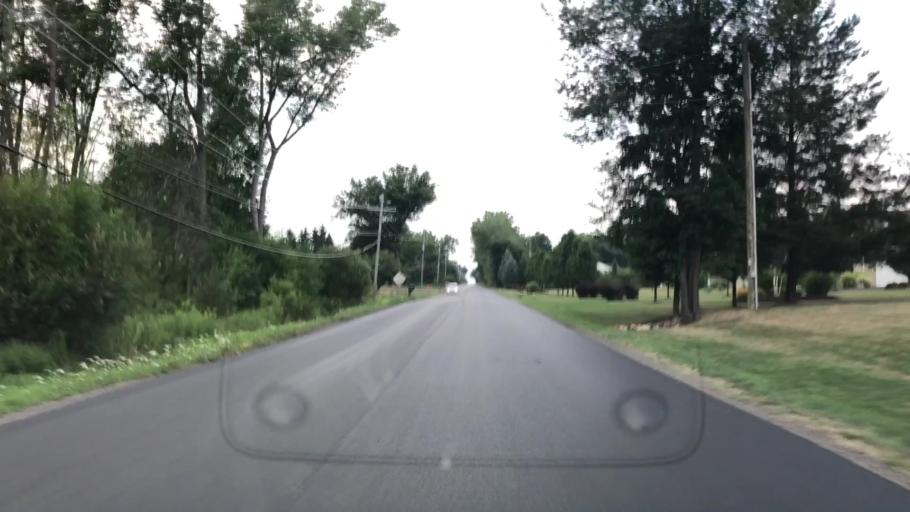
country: US
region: New York
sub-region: Erie County
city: Billington Heights
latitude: 42.8063
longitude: -78.6059
